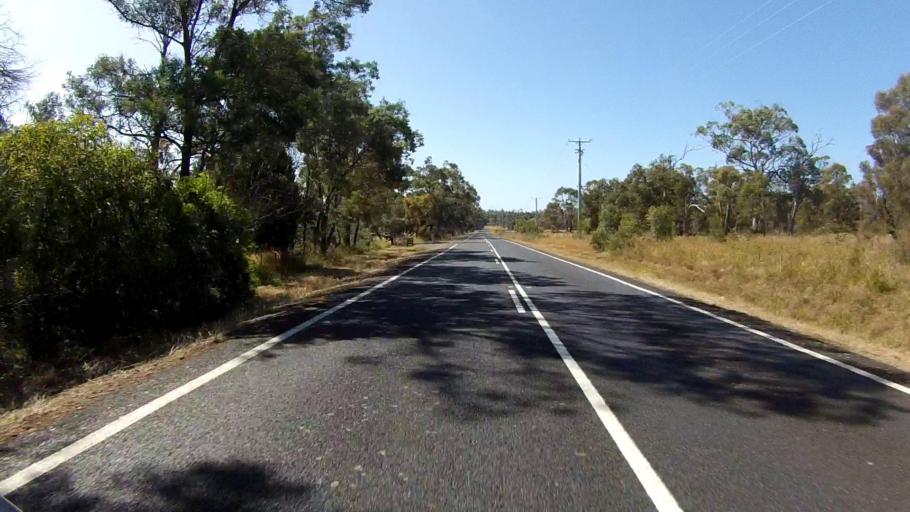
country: AU
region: Tasmania
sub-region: Sorell
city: Sorell
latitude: -42.3878
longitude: 147.9355
